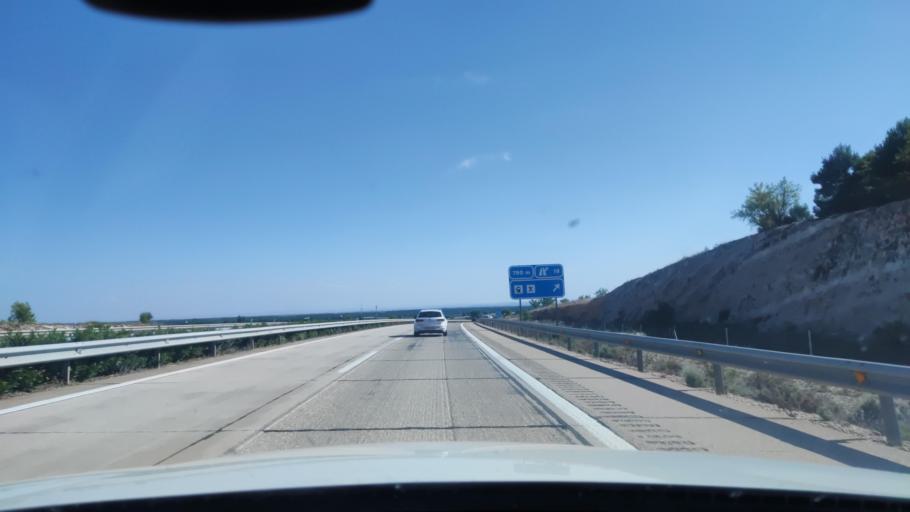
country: ES
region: Castille-La Mancha
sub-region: Provincia de Cuenca
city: Pozoamargo
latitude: 39.3724
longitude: -2.1997
